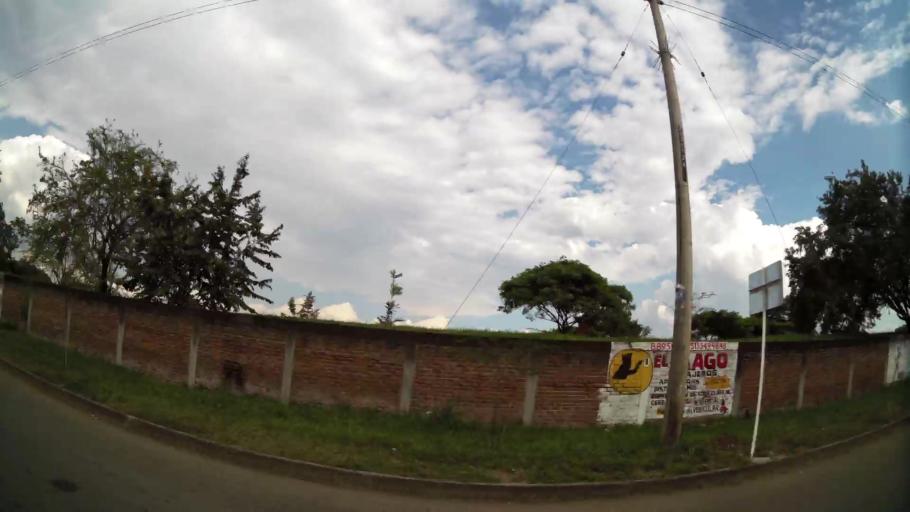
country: CO
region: Valle del Cauca
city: Cali
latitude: 3.4672
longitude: -76.5188
